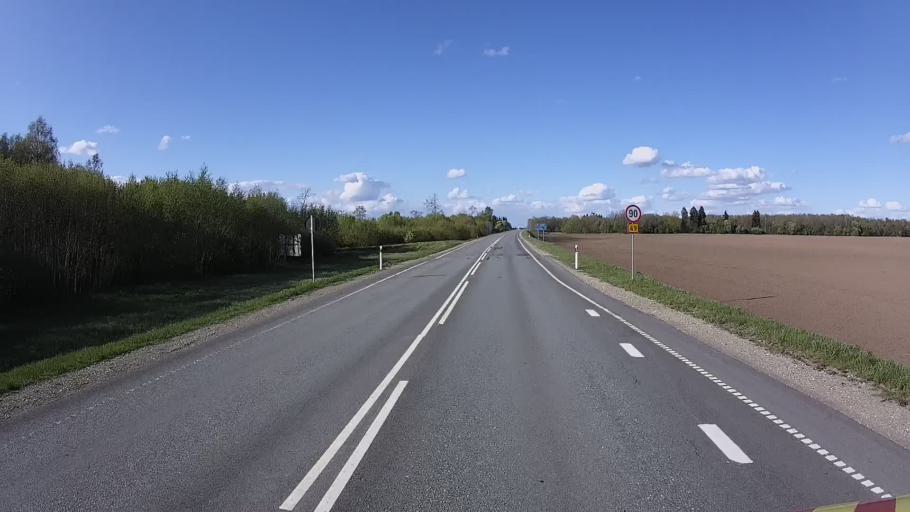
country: EE
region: Viljandimaa
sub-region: Vohma linn
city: Vohma
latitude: 58.6319
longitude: 25.6051
